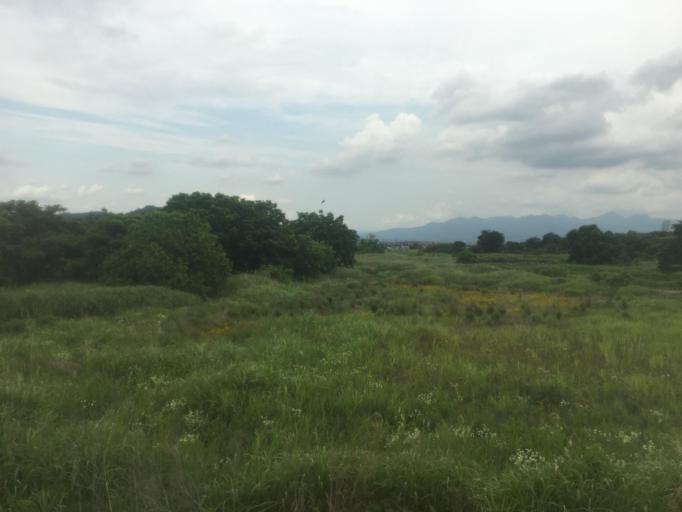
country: JP
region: Gunma
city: Takasaki
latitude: 36.2997
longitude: 139.0156
